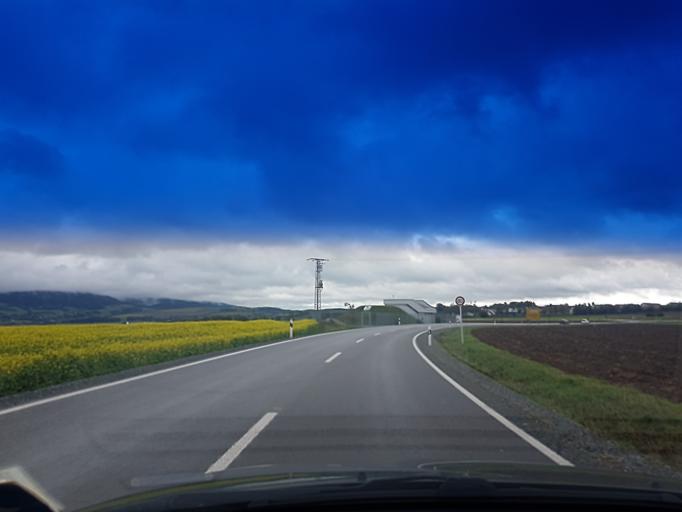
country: DE
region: Bavaria
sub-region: Upper Franconia
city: Bindlach
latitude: 50.0050
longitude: 11.6225
